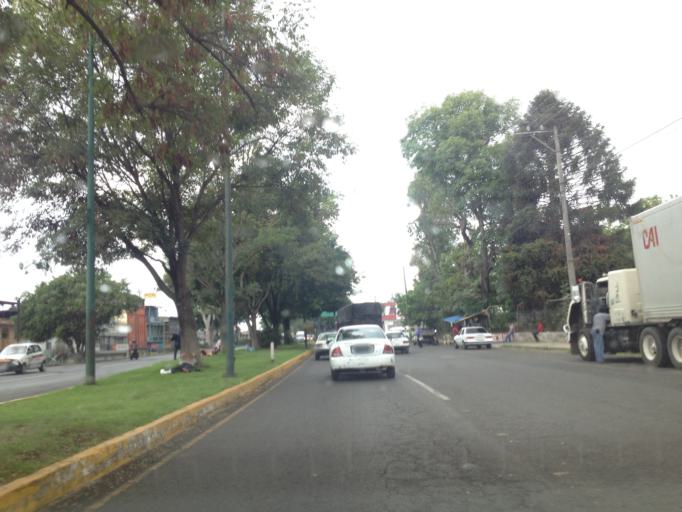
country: MX
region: Michoacan
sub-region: Uruapan
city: Uruapan
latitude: 19.4262
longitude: -102.0420
